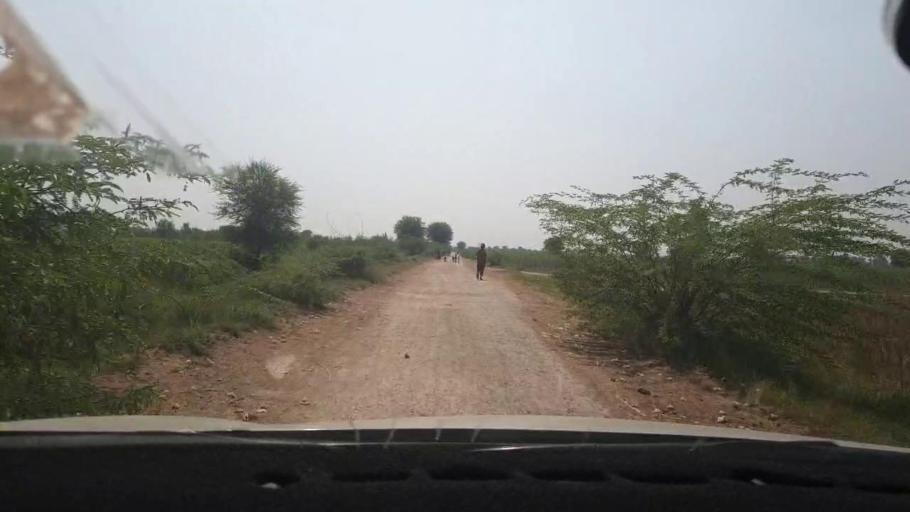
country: PK
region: Sindh
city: Tando Mittha Khan
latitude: 25.9339
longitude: 69.2247
